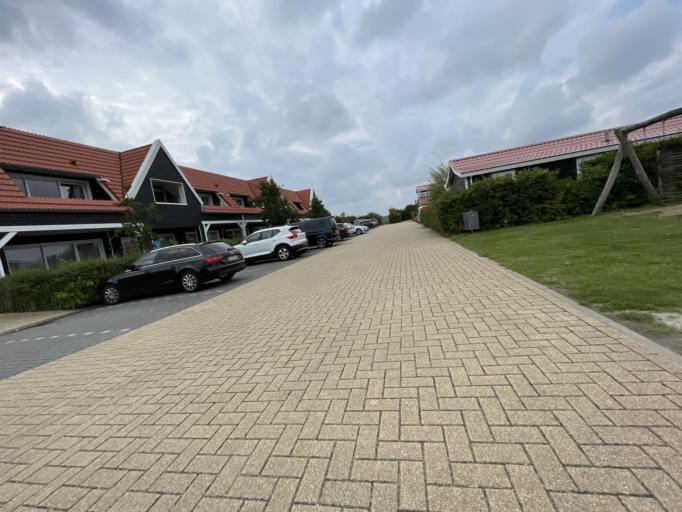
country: NL
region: Zeeland
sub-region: Schouwen-Duiveland
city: Renesse
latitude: 51.7369
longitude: 3.8023
